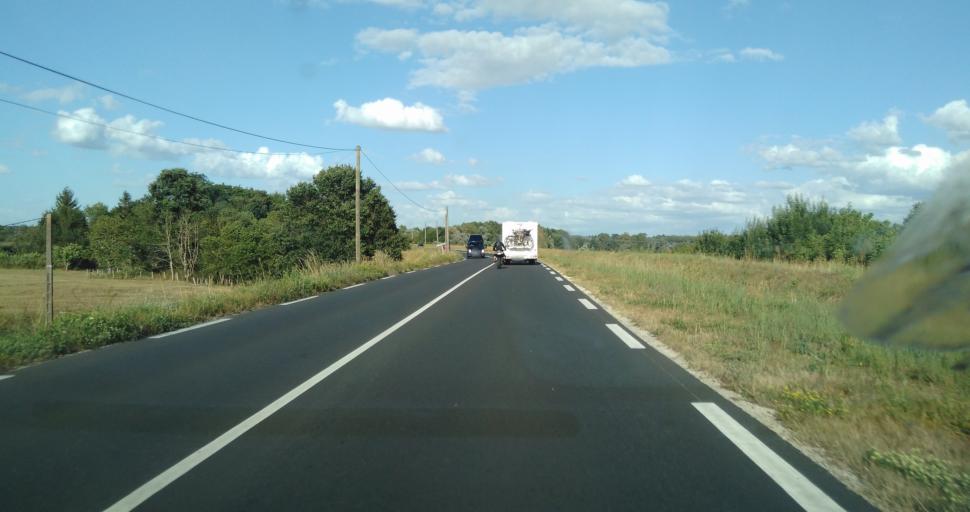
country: FR
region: Centre
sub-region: Departement d'Indre-et-Loire
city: Nazelles-Negron
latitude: 47.4068
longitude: 0.9408
